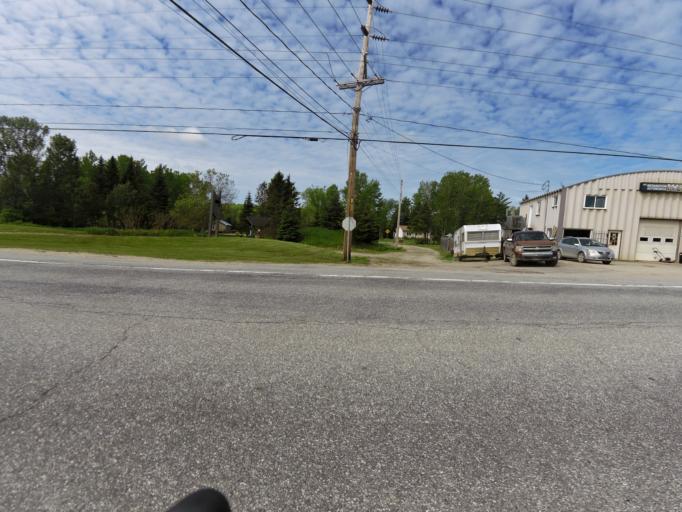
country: CA
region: Quebec
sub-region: Outaouais
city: Wakefield
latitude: 45.8111
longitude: -75.9521
